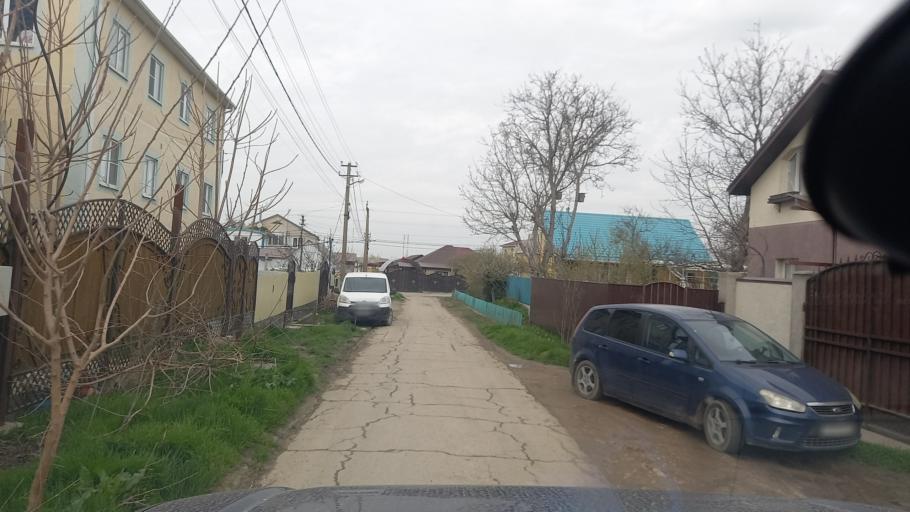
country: RU
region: Krasnodarskiy
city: Tsibanobalka
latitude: 44.9672
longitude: 37.3201
